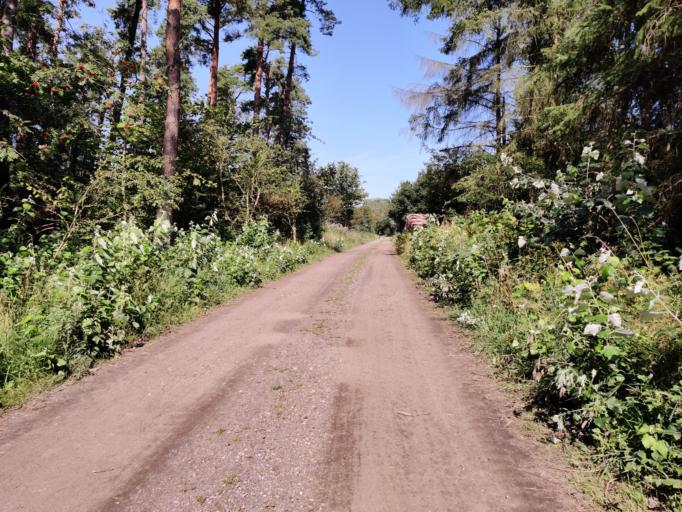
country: DK
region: Zealand
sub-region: Guldborgsund Kommune
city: Nykobing Falster
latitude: 54.6103
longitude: 11.9559
